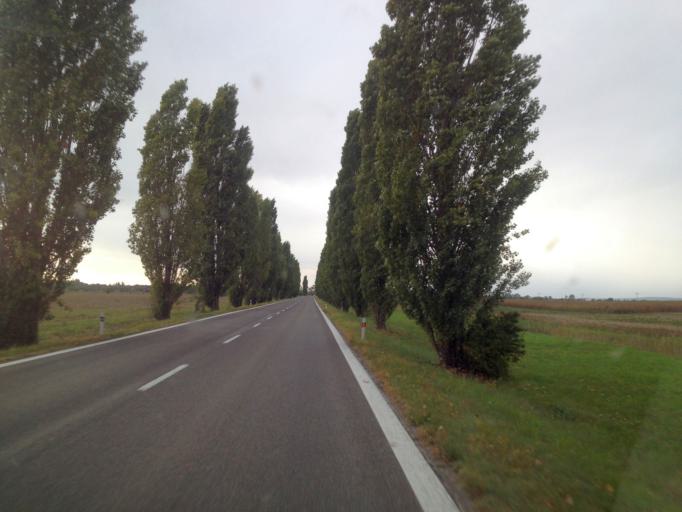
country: HU
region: Komarom-Esztergom
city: Labatlan
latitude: 47.7620
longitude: 18.5105
